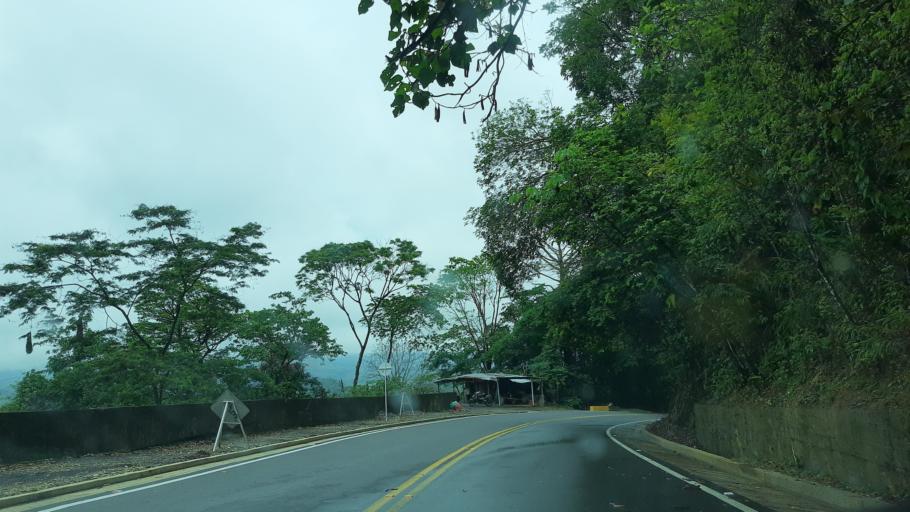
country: CO
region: Casanare
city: Sabanalarga
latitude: 4.7628
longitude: -73.0285
